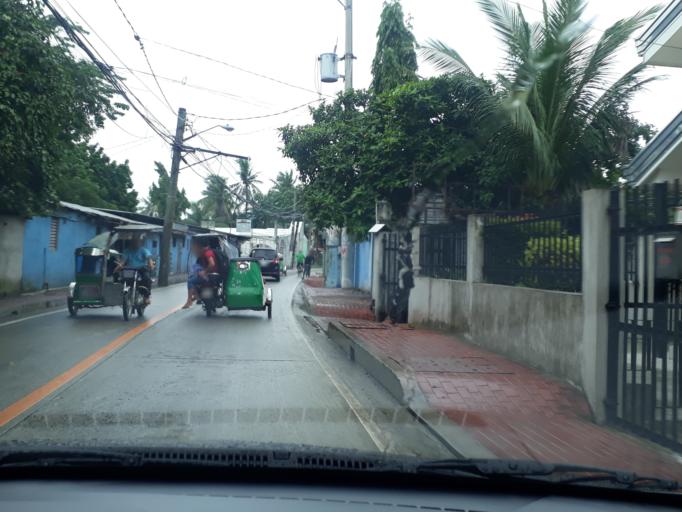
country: PH
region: Calabarzon
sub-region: Province of Rizal
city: Valenzuela
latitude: 14.7113
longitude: 120.9907
